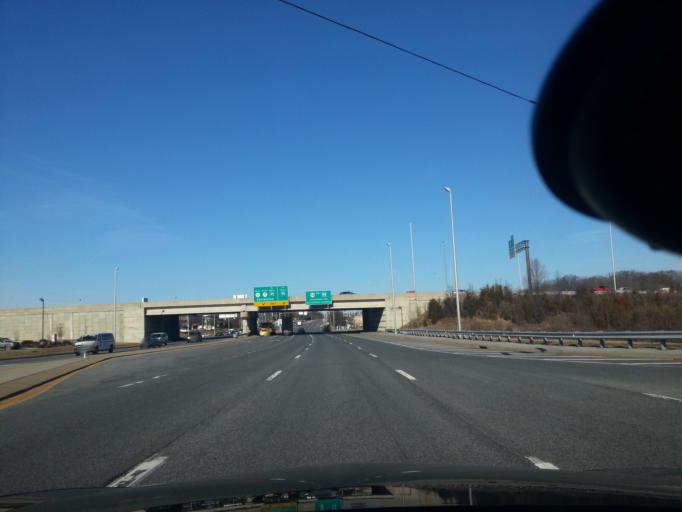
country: US
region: Delaware
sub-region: New Castle County
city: Newport
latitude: 39.6885
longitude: -75.6530
